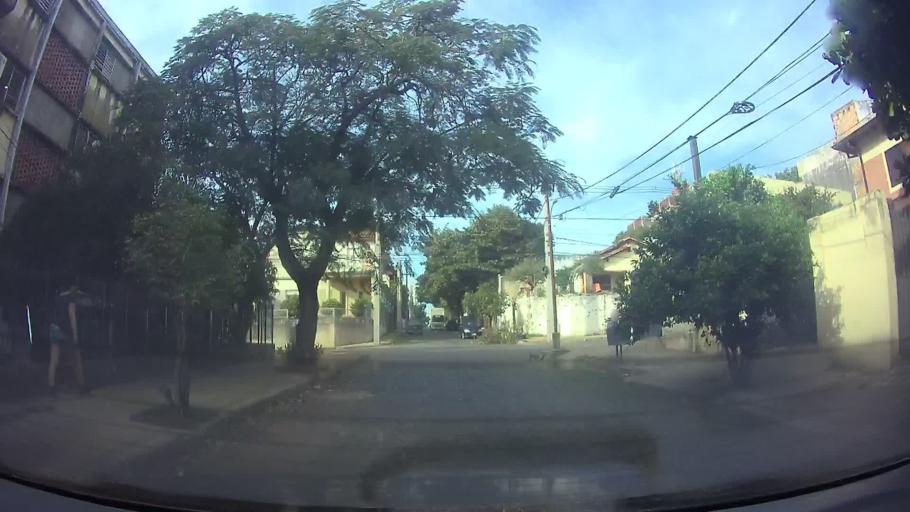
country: PY
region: Presidente Hayes
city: Nanawa
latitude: -25.2829
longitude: -57.6564
